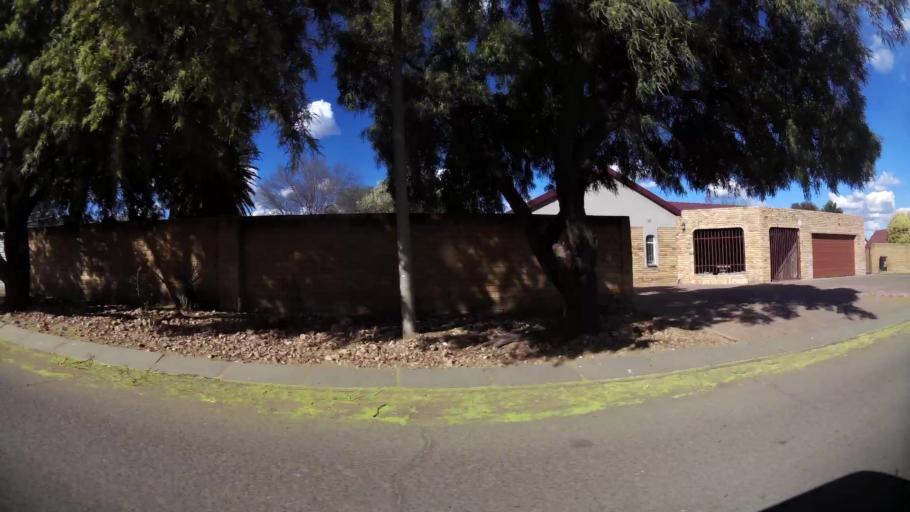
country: ZA
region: North-West
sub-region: Dr Kenneth Kaunda District Municipality
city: Klerksdorp
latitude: -26.8215
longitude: 26.6501
